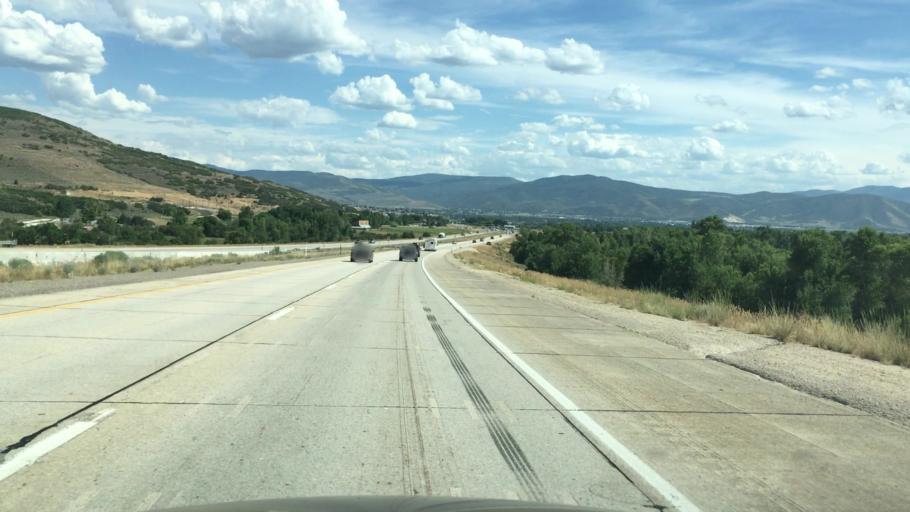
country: US
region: Utah
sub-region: Wasatch County
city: Heber
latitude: 40.5701
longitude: -111.4311
